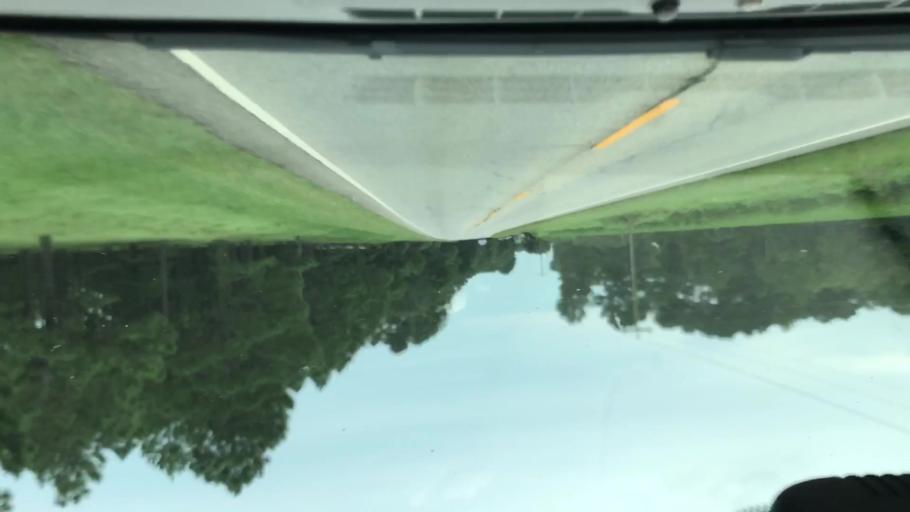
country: US
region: Georgia
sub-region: Early County
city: Blakely
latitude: 31.3613
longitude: -84.9664
